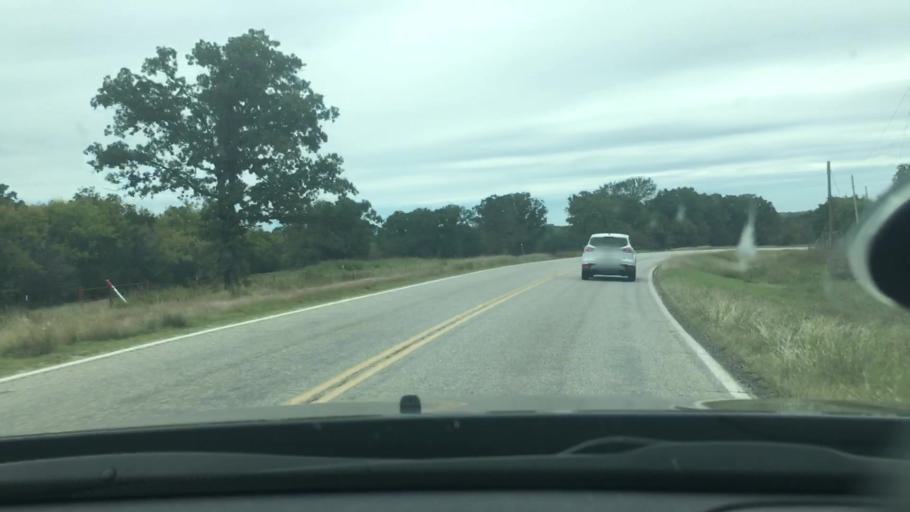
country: US
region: Oklahoma
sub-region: Johnston County
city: Tishomingo
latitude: 34.3207
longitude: -96.4247
